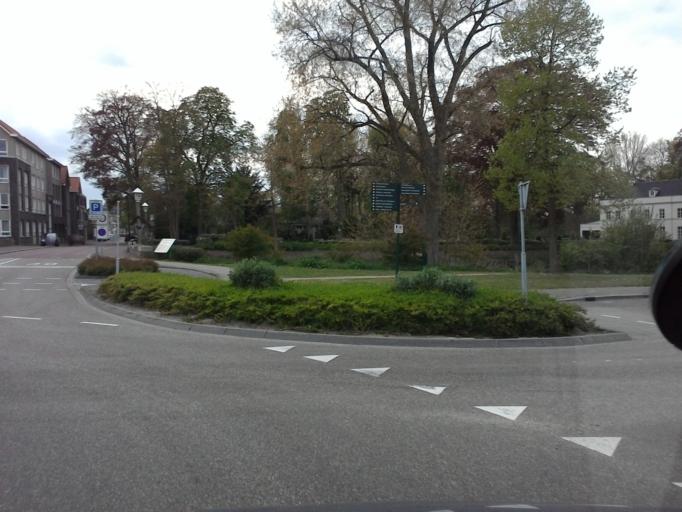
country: NL
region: North Brabant
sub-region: Gemeente Sint-Oedenrode
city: Sint-Oedenrode
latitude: 51.5655
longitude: 5.4658
